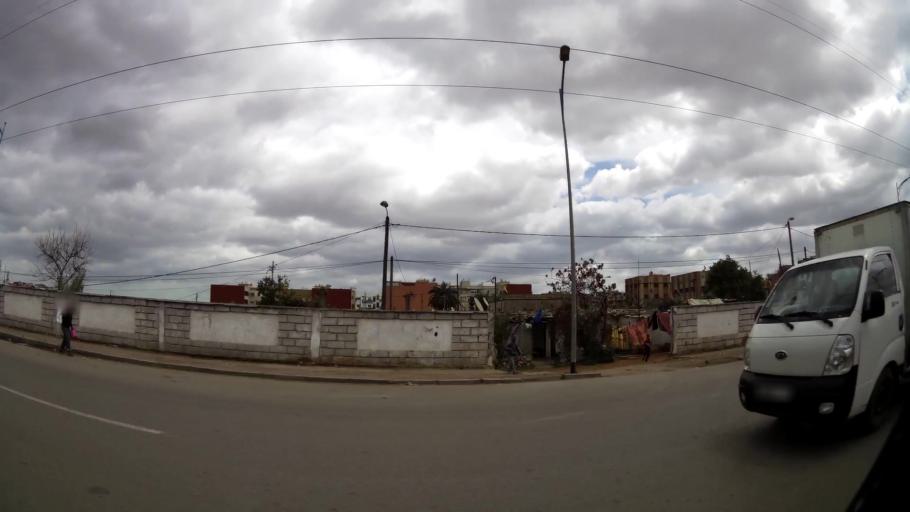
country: MA
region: Grand Casablanca
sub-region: Mediouna
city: Tit Mellil
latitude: 33.5826
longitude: -7.5446
